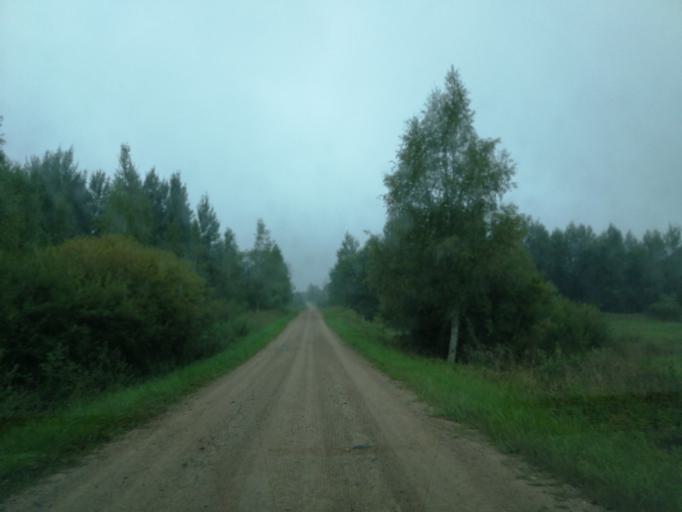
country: LV
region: Preilu Rajons
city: Jaunaglona
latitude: 56.3195
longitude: 27.0149
